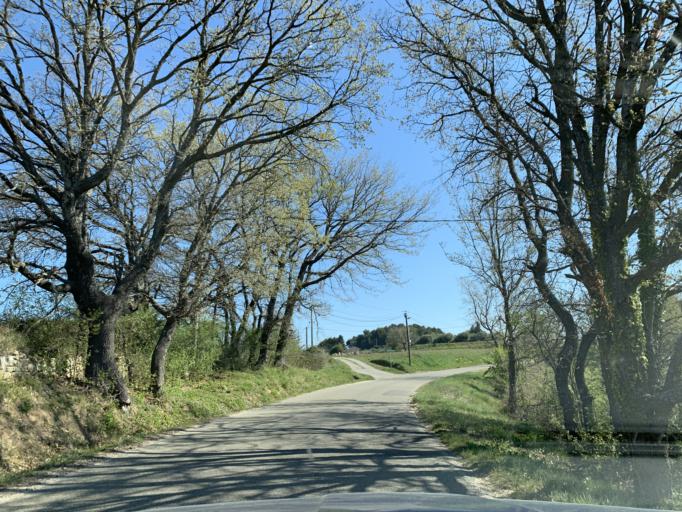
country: FR
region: Provence-Alpes-Cote d'Azur
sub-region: Departement du Vaucluse
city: Goult
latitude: 43.8771
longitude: 5.2535
